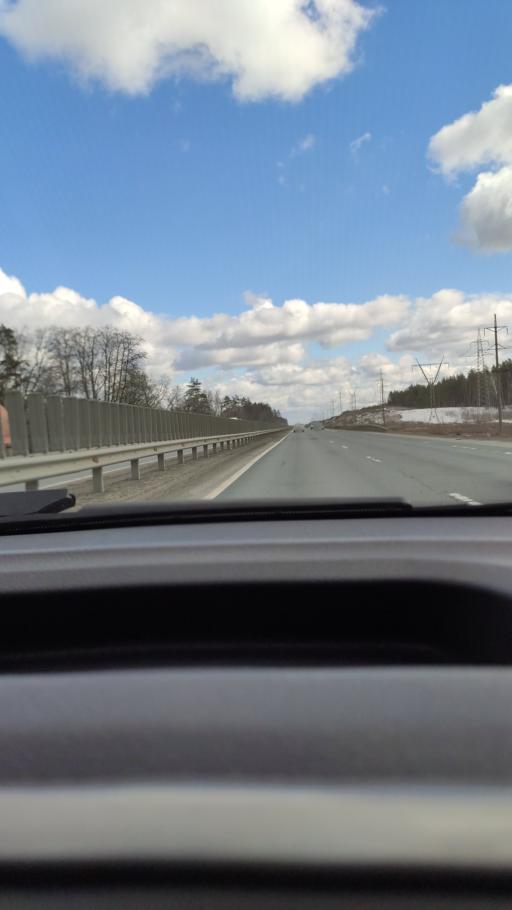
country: RU
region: Samara
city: Pribrezhnyy
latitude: 53.5148
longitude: 49.8814
